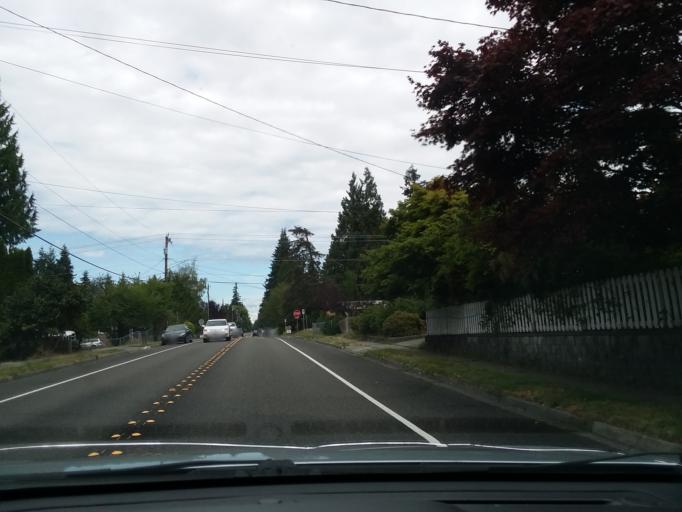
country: US
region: Washington
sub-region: Snohomish County
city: Alderwood Manor
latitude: 47.8240
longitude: -122.2978
